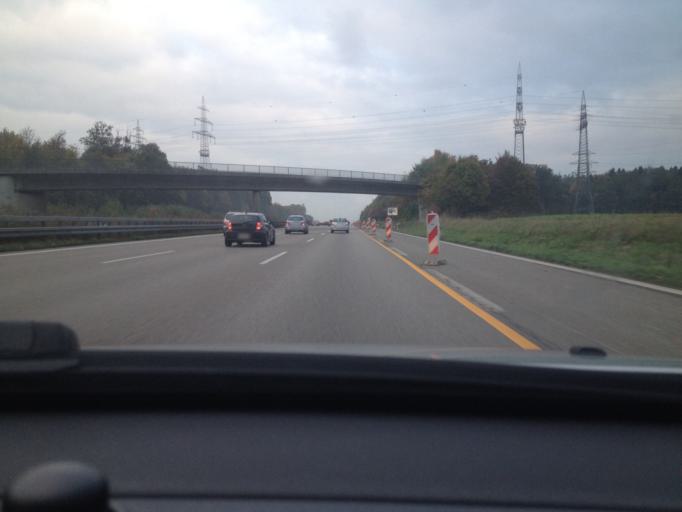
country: DE
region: Baden-Wuerttemberg
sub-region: Regierungsbezirk Stuttgart
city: Wendlingen am Neckar
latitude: 48.6541
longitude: 9.3916
